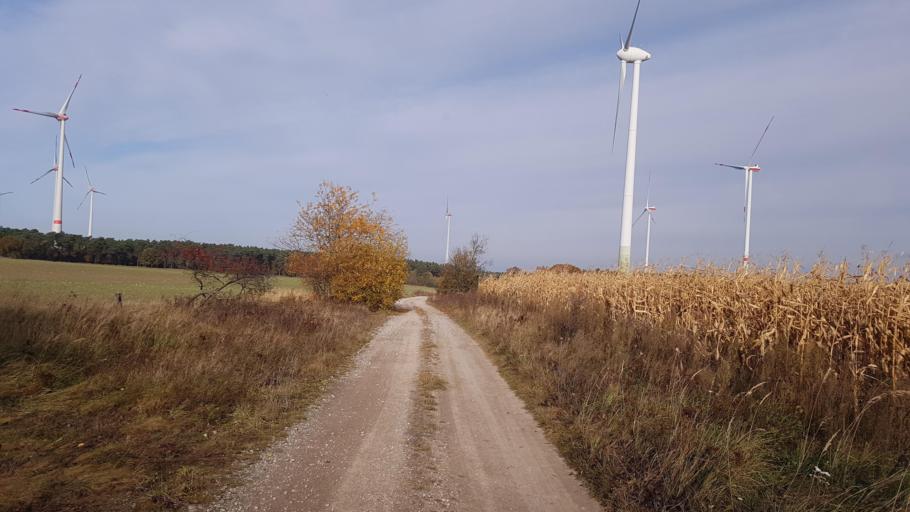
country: DE
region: Brandenburg
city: Treuenbrietzen
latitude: 52.0100
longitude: 12.8797
